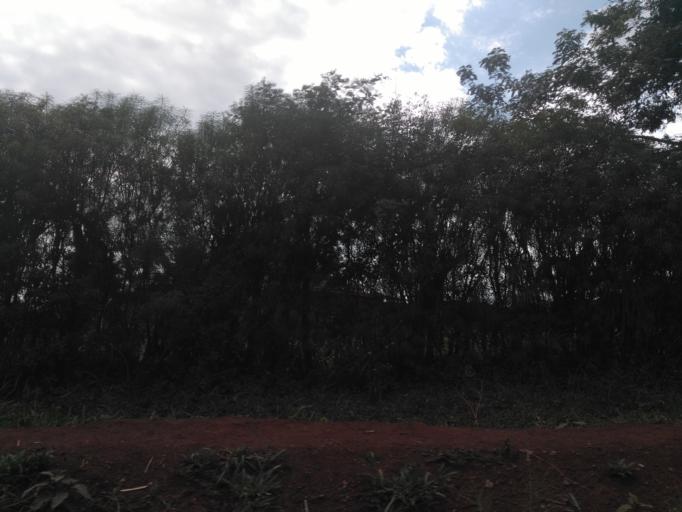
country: UG
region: Central Region
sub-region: Buikwe District
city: Njeru
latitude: 0.4218
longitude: 33.1875
